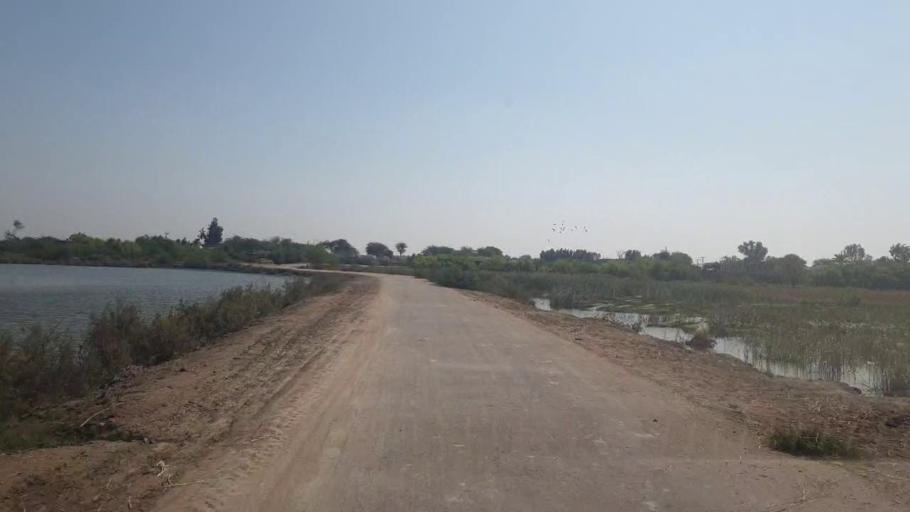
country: PK
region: Sindh
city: Badin
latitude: 24.6401
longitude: 68.9127
